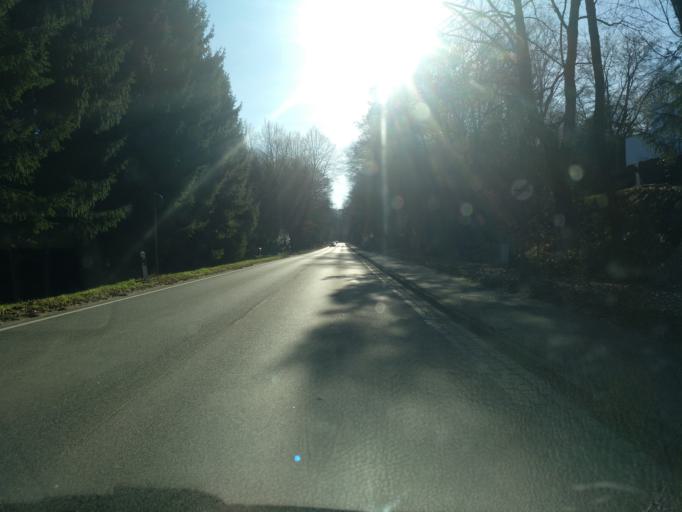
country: DE
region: Hamburg
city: Harburg
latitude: 53.4505
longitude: 9.9050
